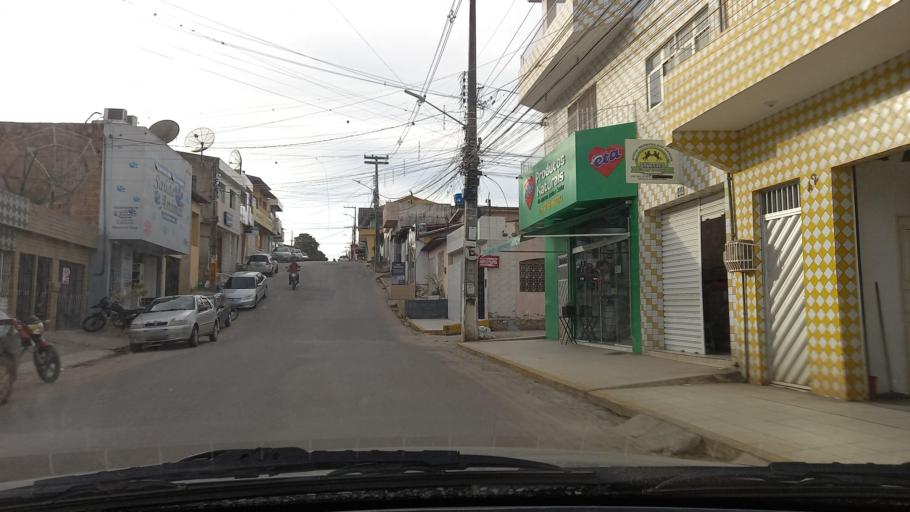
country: BR
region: Pernambuco
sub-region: Gravata
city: Gravata
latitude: -8.1986
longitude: -35.5628
